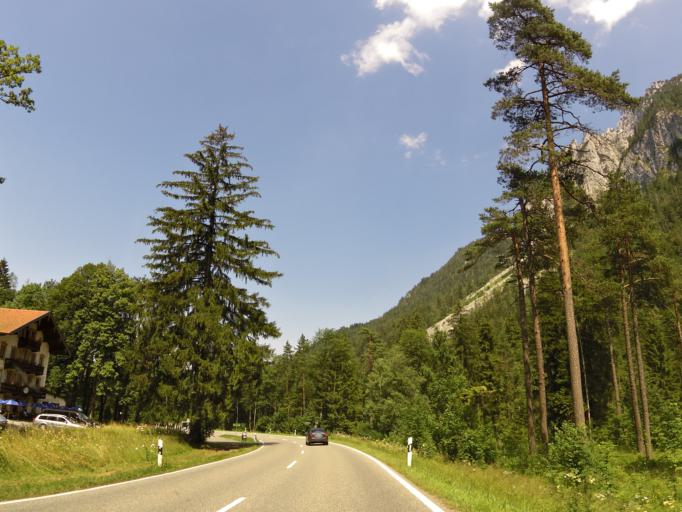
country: DE
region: Bavaria
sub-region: Upper Bavaria
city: Ruhpolding
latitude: 47.7308
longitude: 12.6626
